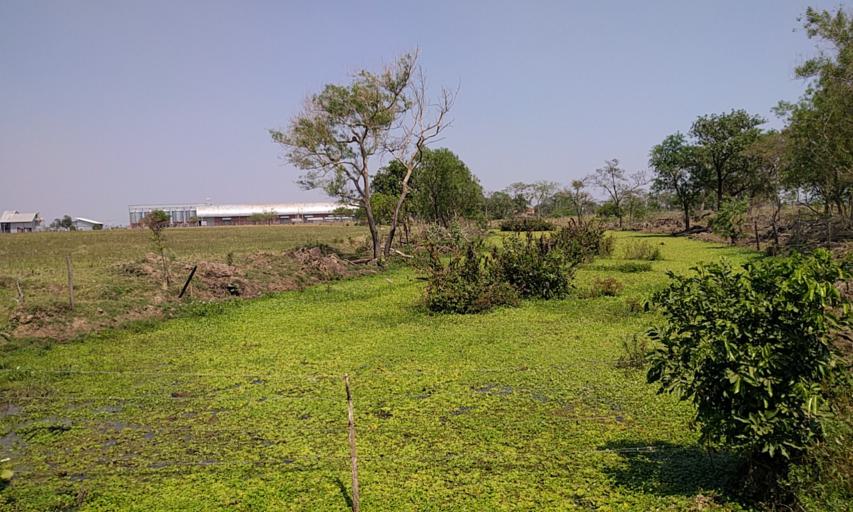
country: BO
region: Santa Cruz
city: Warnes
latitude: -17.4497
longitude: -63.1867
